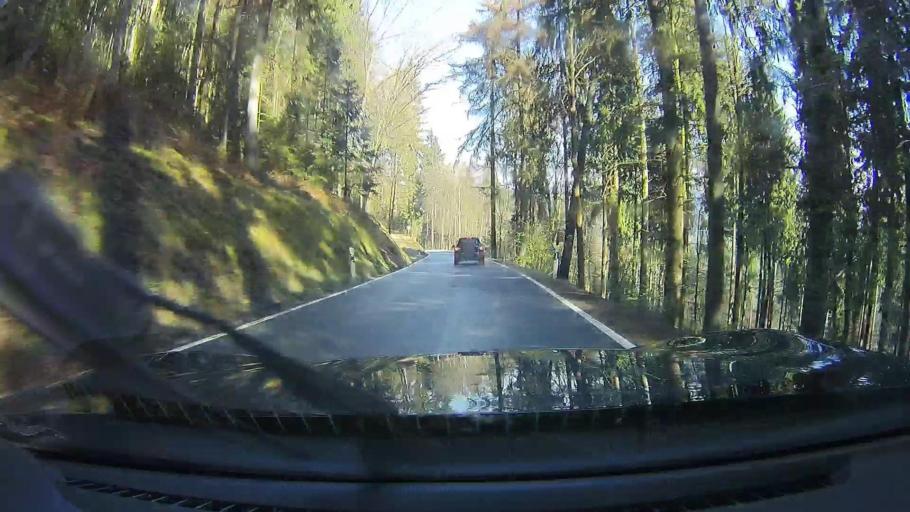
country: DE
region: Hesse
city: Hirschhorn
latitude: 49.4298
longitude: 8.9089
